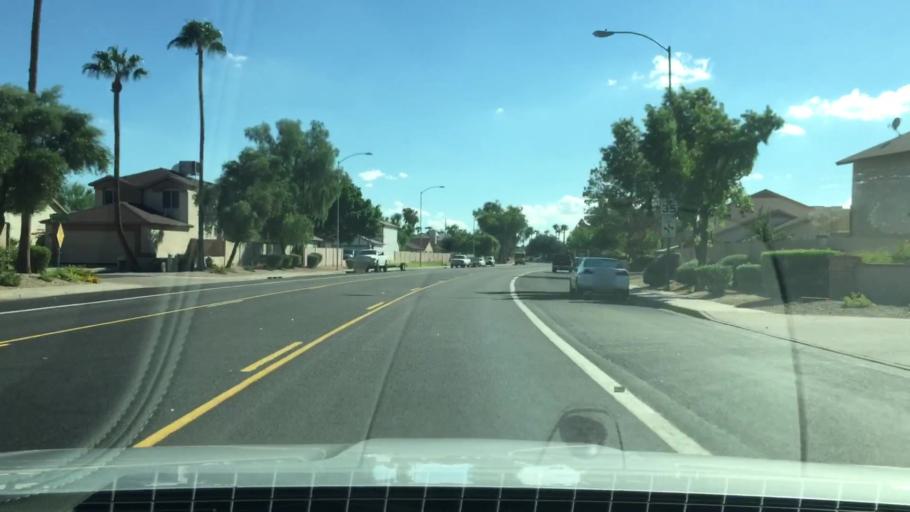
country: US
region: Arizona
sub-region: Maricopa County
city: Gilbert
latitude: 33.3829
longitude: -111.7475
